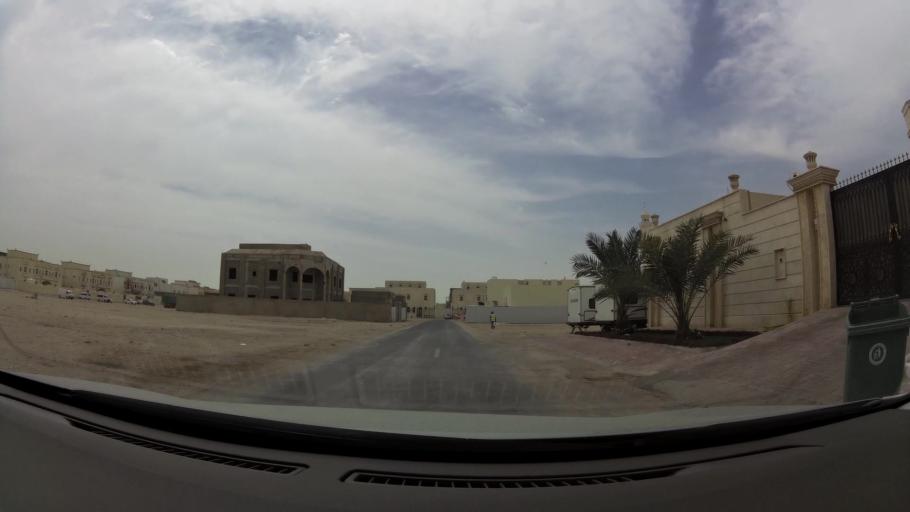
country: QA
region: Baladiyat ad Dawhah
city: Doha
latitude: 25.2083
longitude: 51.4648
